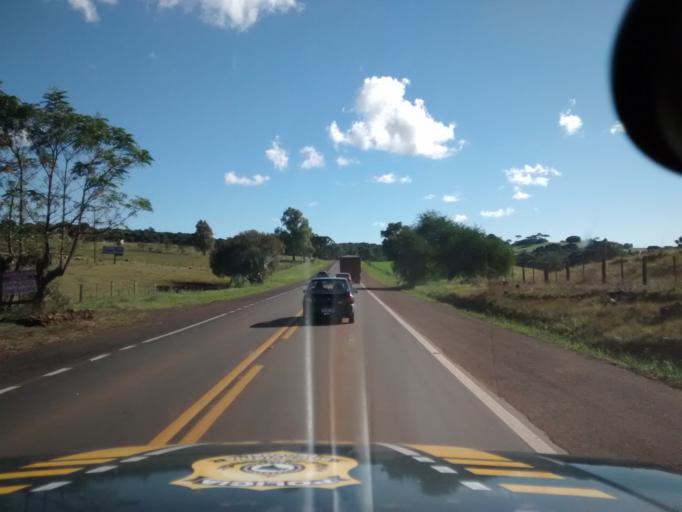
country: BR
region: Rio Grande do Sul
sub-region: Lagoa Vermelha
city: Lagoa Vermelha
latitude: -28.2935
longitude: -51.4405
